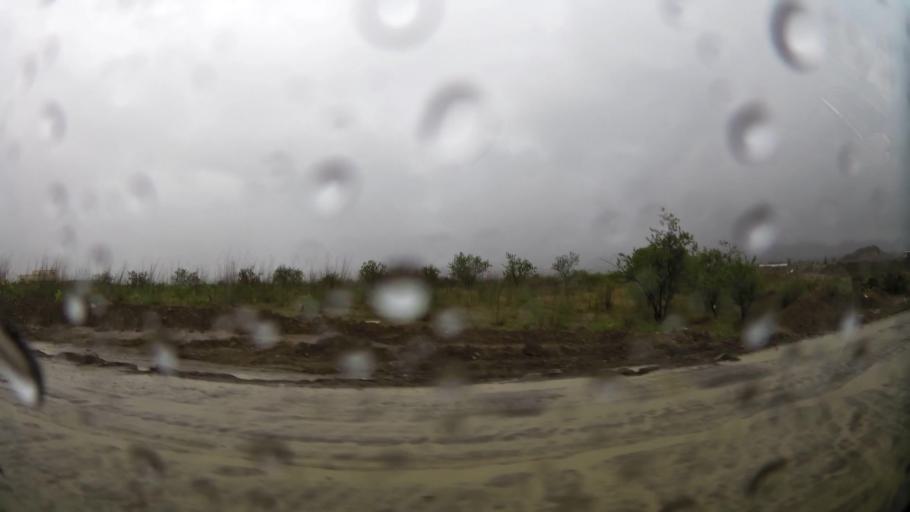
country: MA
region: Oriental
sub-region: Nador
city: Midar
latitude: 34.8673
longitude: -3.7250
